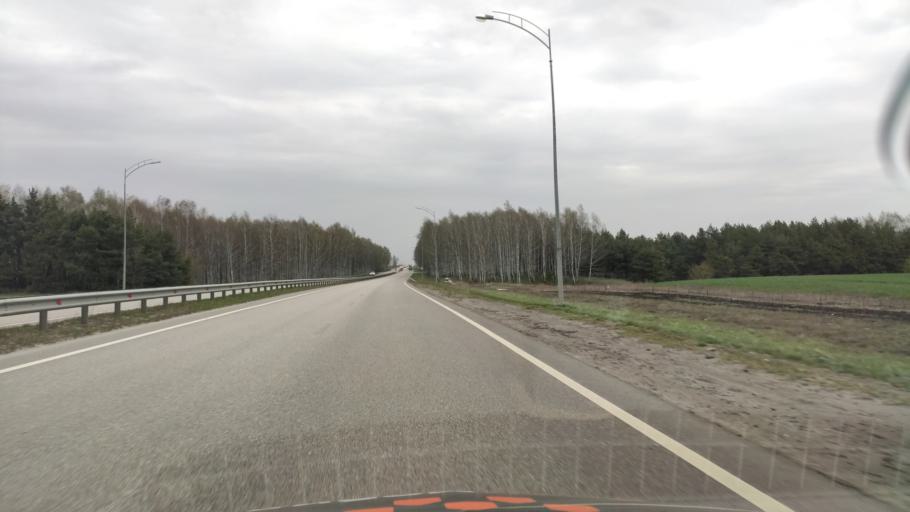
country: RU
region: Belgorod
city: Staryy Oskol
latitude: 51.4067
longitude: 37.8804
